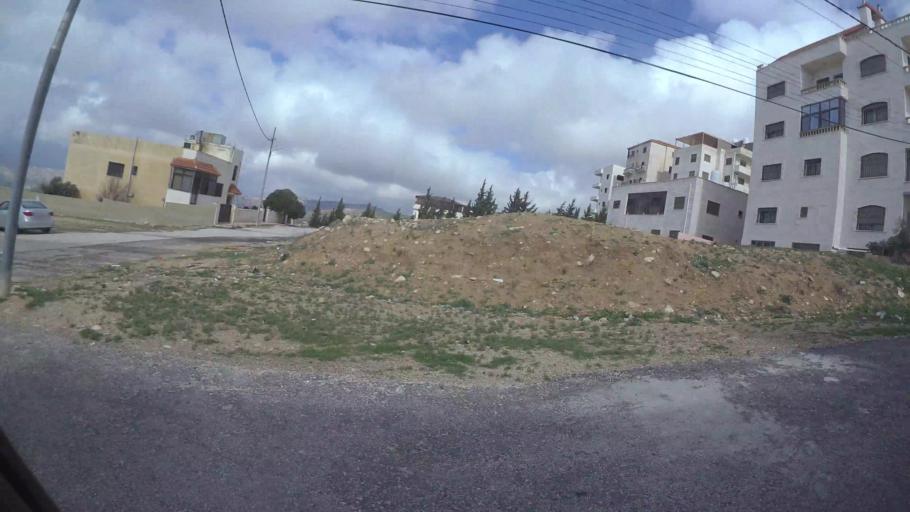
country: JO
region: Amman
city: Al Jubayhah
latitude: 32.0707
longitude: 35.8773
